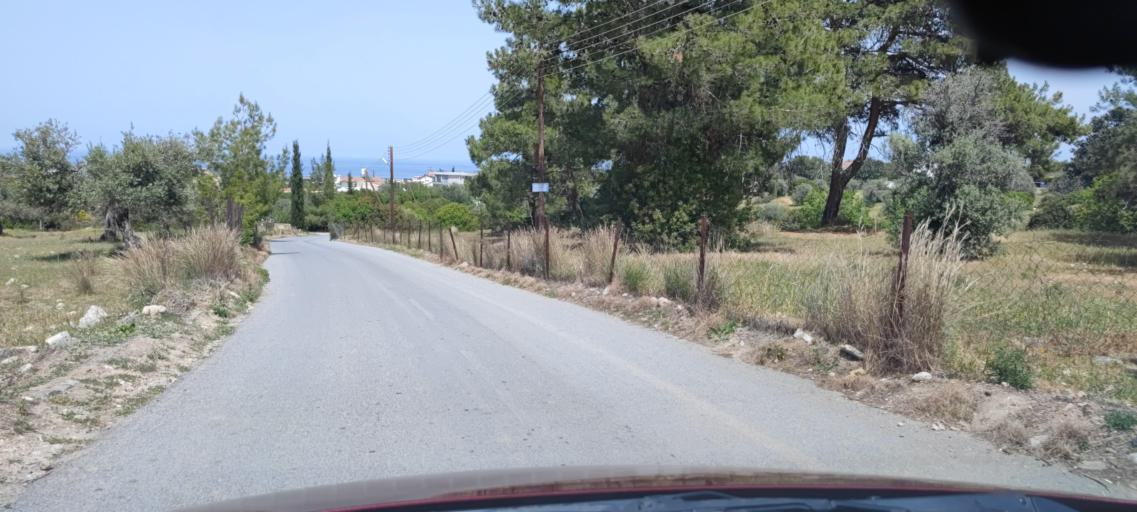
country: CY
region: Keryneia
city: Kyrenia
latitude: 35.3160
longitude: 33.3629
